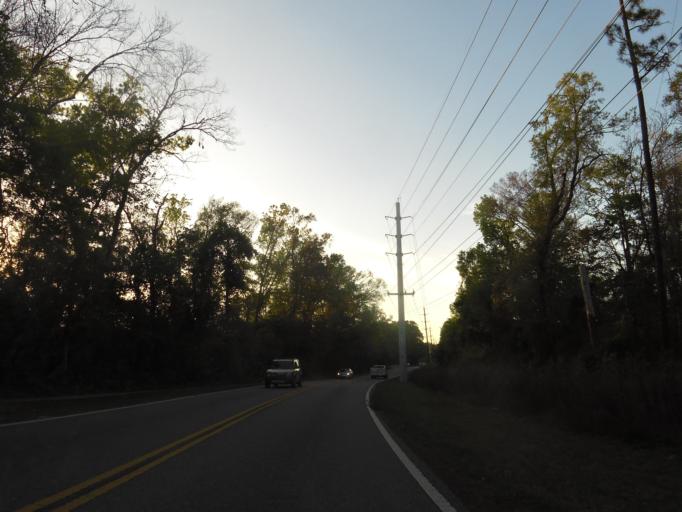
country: US
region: Florida
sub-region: Duval County
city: Jacksonville
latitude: 30.2801
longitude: -81.5708
